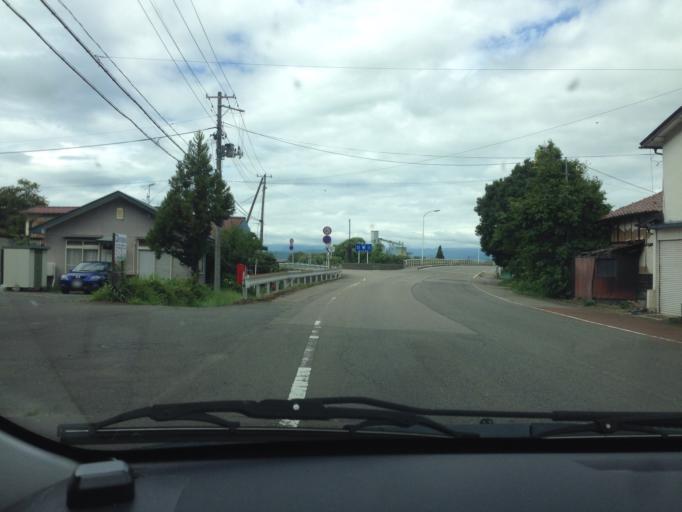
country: JP
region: Fukushima
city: Kitakata
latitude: 37.5887
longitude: 139.8887
